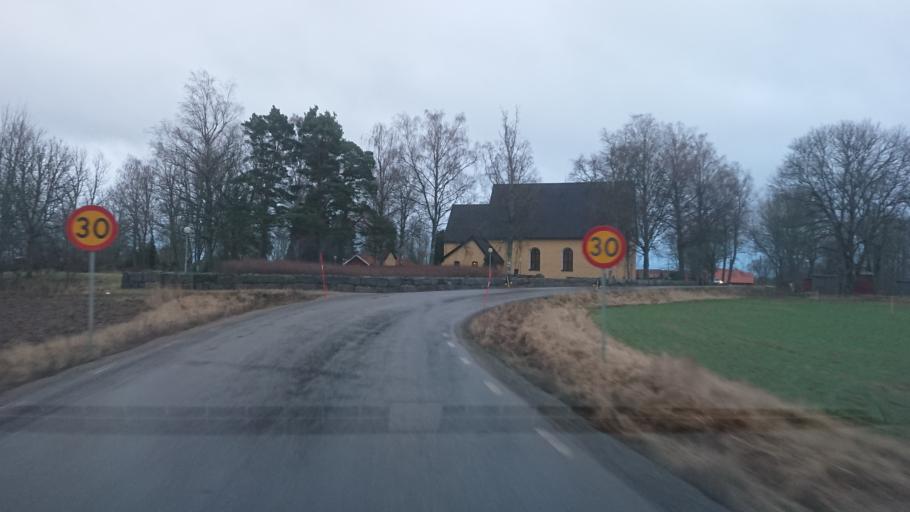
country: SE
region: Uppsala
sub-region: Uppsala Kommun
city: Gamla Uppsala
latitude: 59.9567
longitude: 17.6056
